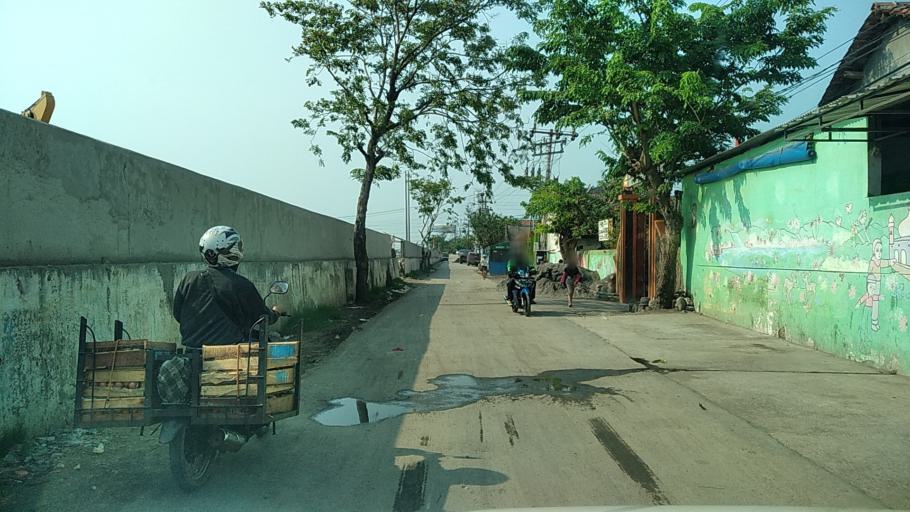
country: ID
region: Central Java
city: Semarang
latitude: -6.9571
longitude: 110.4419
